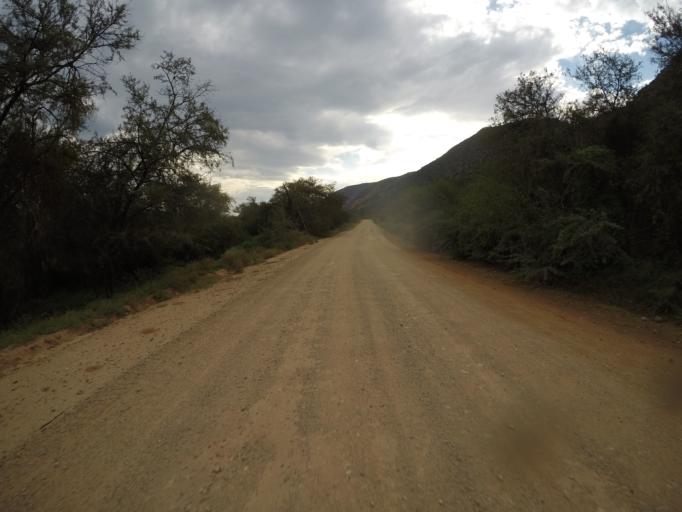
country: ZA
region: Eastern Cape
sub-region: Cacadu District Municipality
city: Kareedouw
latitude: -33.5748
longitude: 24.1381
